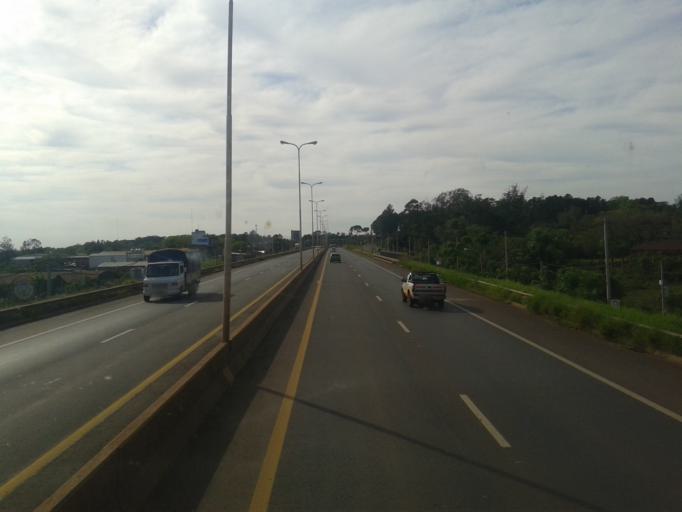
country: AR
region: Misiones
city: Garupa
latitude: -27.4586
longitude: -55.8515
